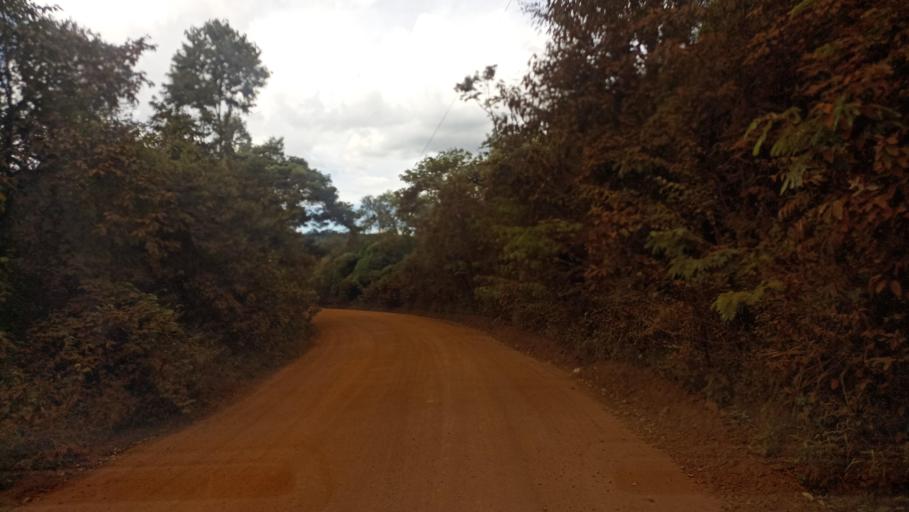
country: BR
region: Minas Gerais
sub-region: Itabirito
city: Itabirito
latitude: -20.3630
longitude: -43.7644
